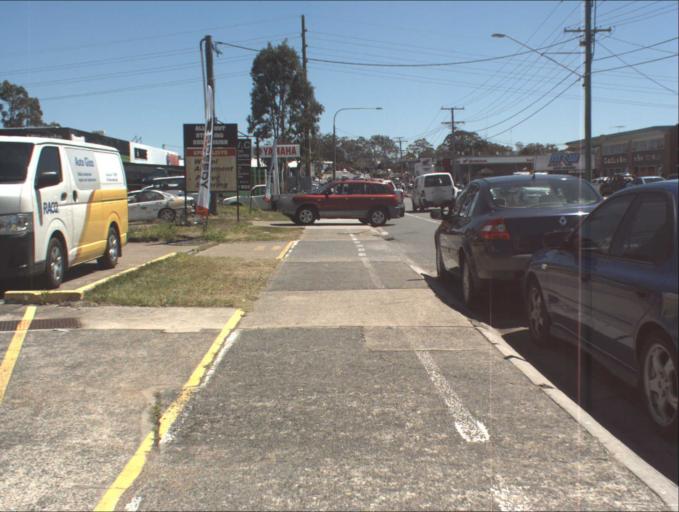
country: AU
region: Queensland
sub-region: Logan
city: Springwood
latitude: -27.6211
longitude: 153.1252
